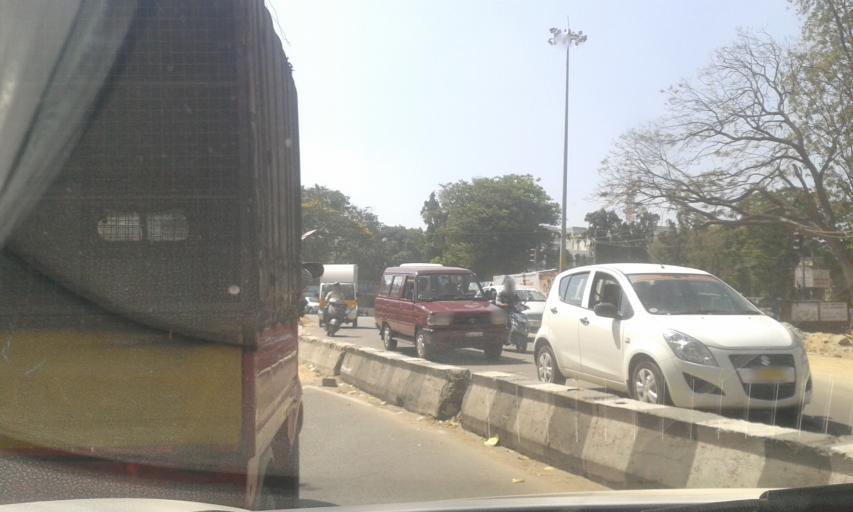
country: IN
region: Karnataka
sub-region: Bangalore Urban
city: Bangalore
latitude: 12.9764
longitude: 77.5646
